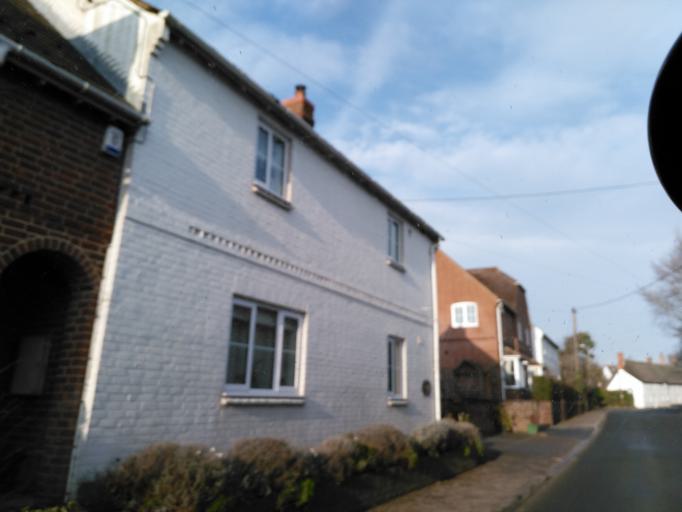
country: GB
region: England
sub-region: Wiltshire
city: Market Lavington
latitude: 51.2792
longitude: -1.9948
